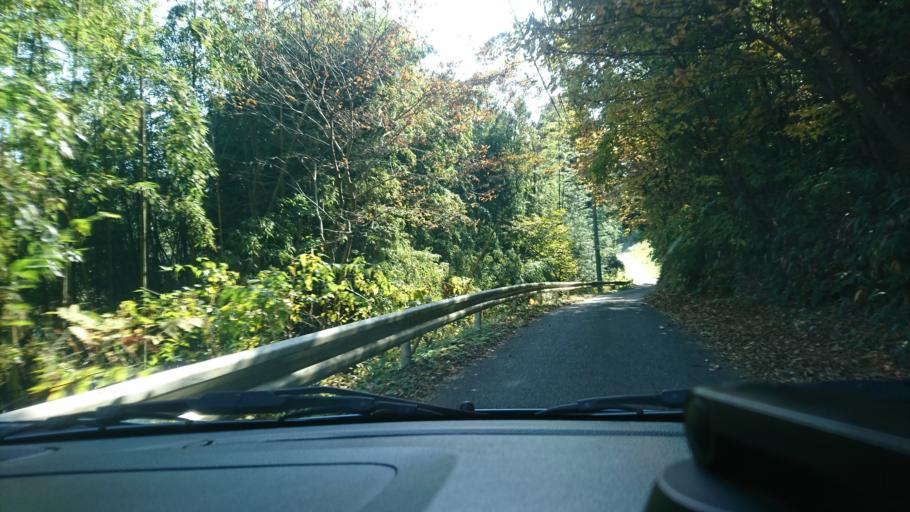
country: JP
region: Iwate
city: Ichinoseki
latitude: 38.7986
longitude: 141.2464
